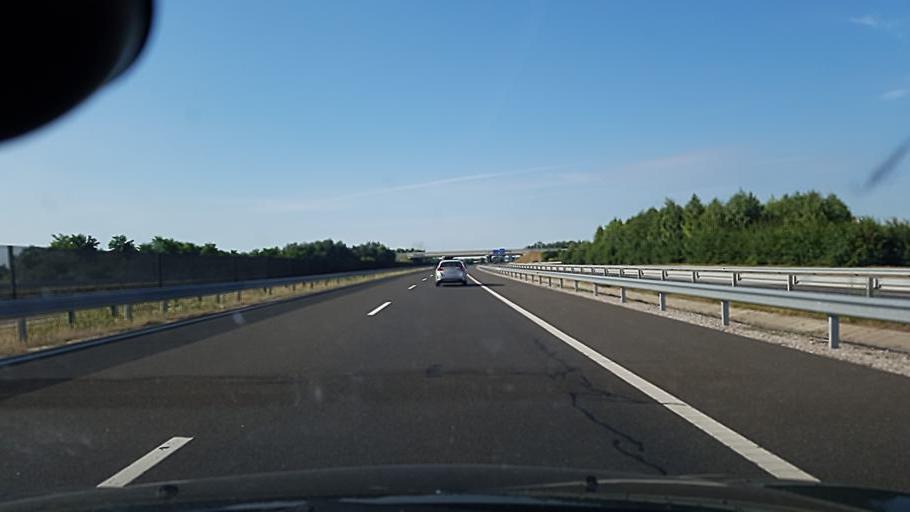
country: HU
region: Fejer
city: Baracs
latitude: 46.9268
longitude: 18.8958
